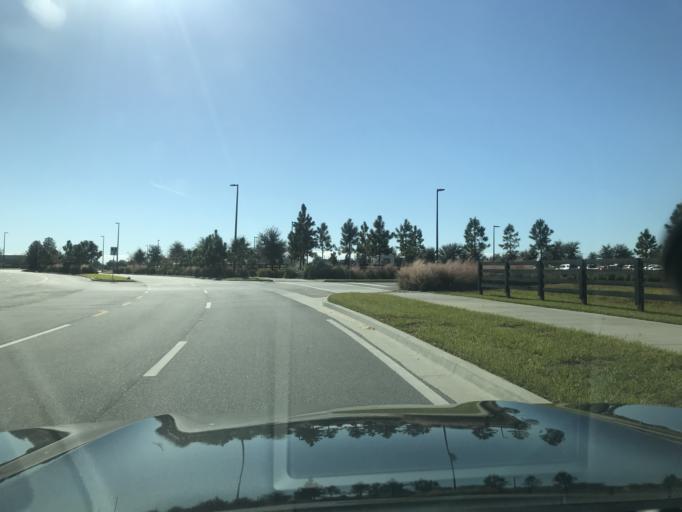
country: US
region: Florida
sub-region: Orange County
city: Oakland
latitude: 28.4786
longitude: -81.6276
